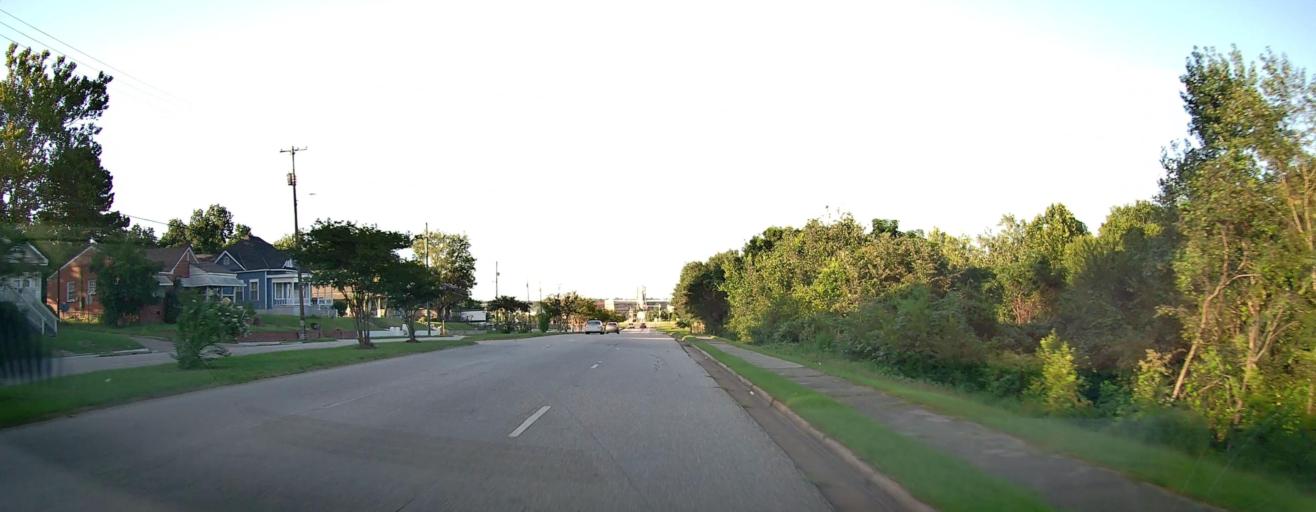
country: US
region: Alabama
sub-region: Russell County
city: Phenix City
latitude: 32.4604
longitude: -85.0022
